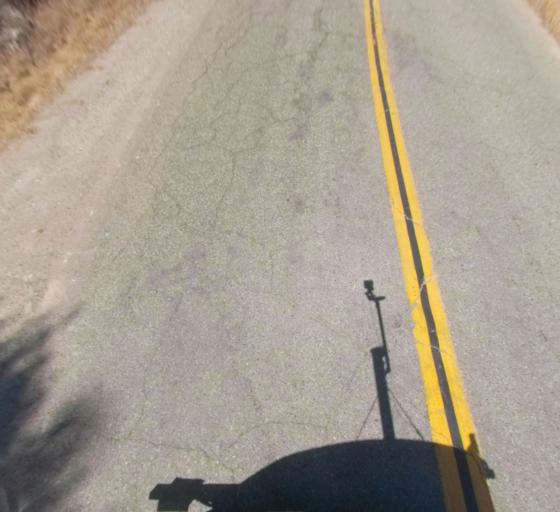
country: US
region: California
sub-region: Fresno County
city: Auberry
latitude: 37.1971
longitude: -119.5006
